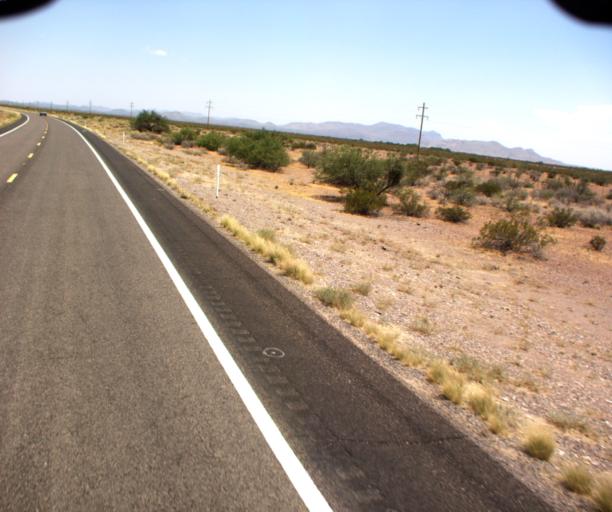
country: US
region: Arizona
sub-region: Graham County
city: Safford
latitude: 32.7825
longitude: -109.5358
